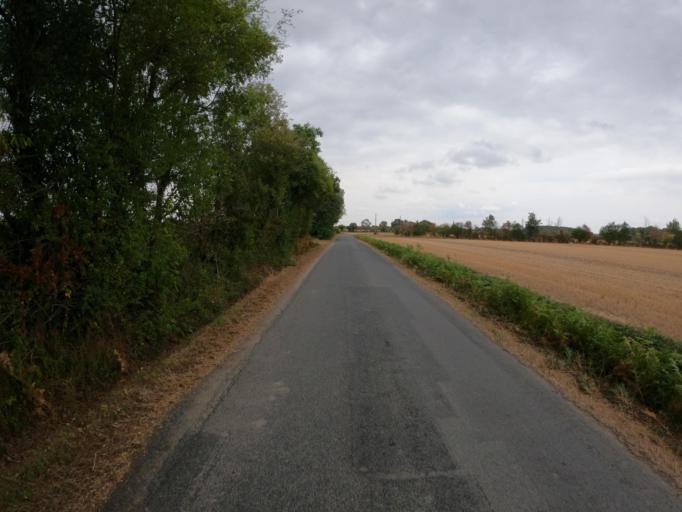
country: FR
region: Pays de la Loire
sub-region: Departement de la Vendee
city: La Bruffiere
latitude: 46.9908
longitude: -1.1578
